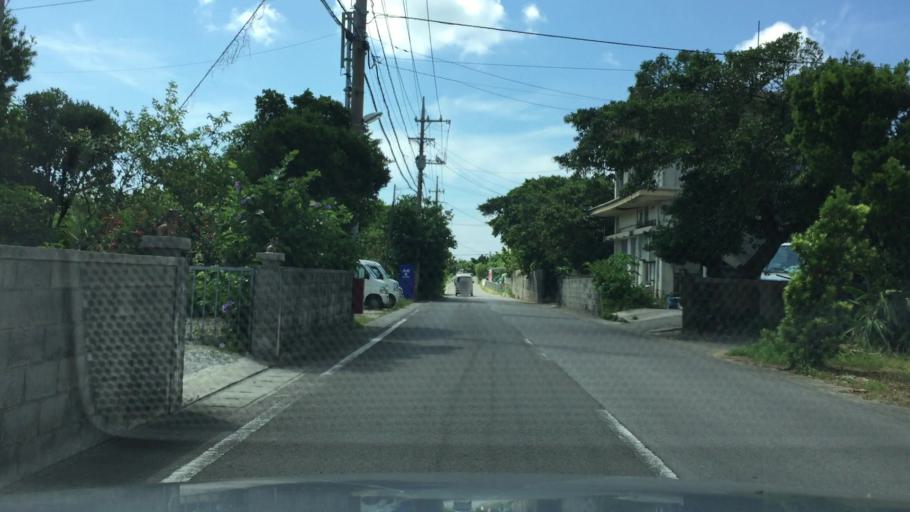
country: JP
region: Okinawa
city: Ishigaki
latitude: 24.3571
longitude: 124.2013
